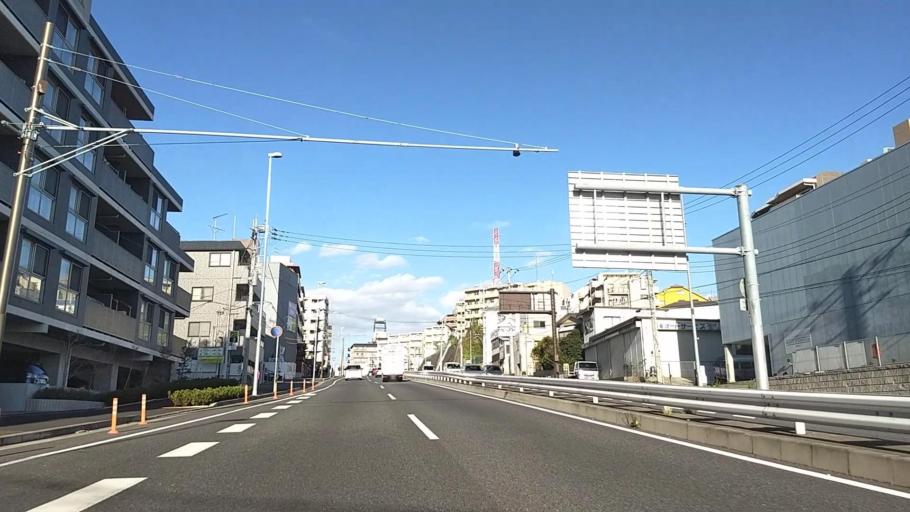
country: JP
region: Tokyo
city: Chofugaoka
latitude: 35.5703
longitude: 139.5665
